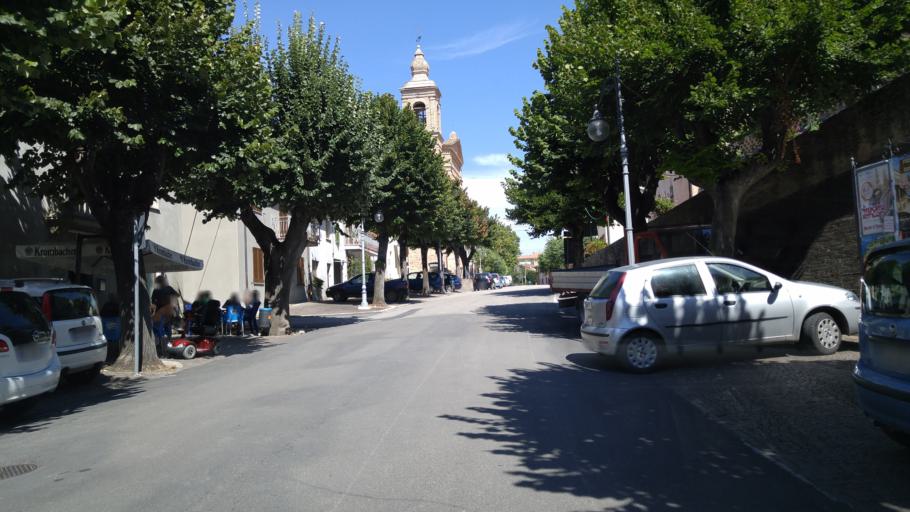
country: IT
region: The Marches
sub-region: Provincia di Pesaro e Urbino
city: San Giorgio di Pesaro
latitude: 43.7167
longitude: 12.9746
